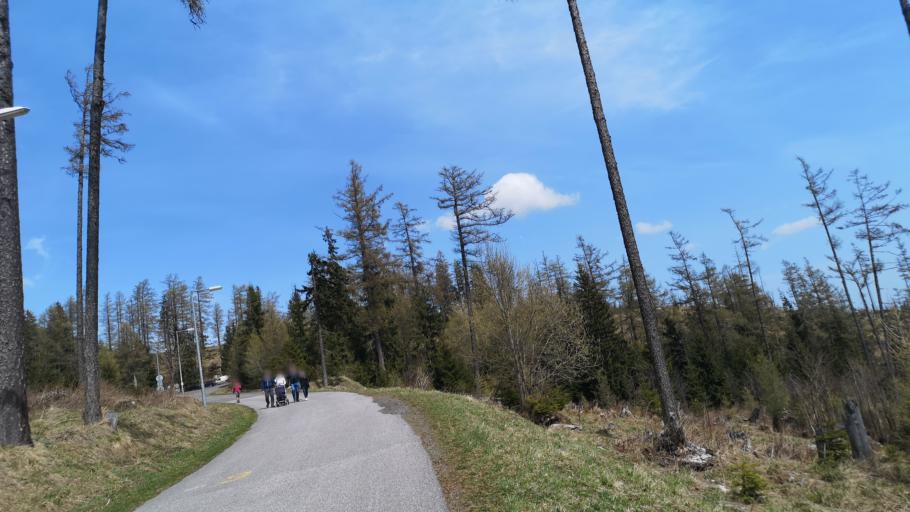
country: SK
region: Presovsky
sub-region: Okres Poprad
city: Vysoke Tatry
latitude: 49.1565
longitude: 20.2256
